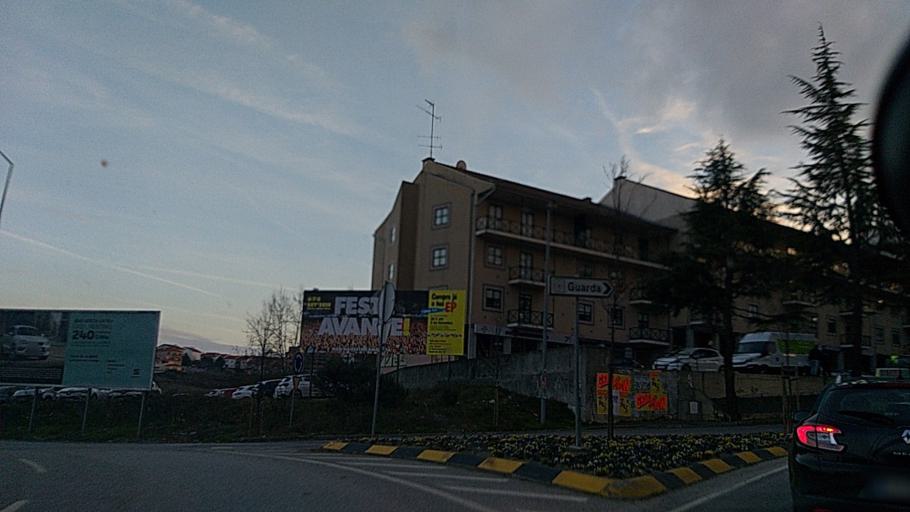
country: PT
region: Guarda
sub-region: Guarda
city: Guarda
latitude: 40.5490
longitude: -7.2489
